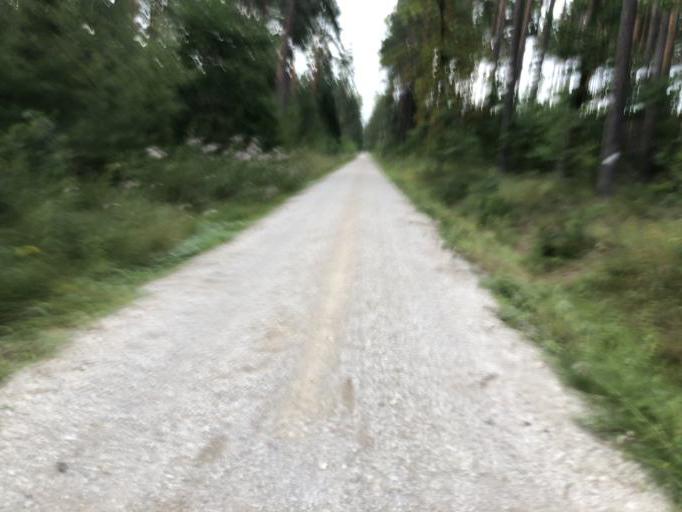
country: DE
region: Bavaria
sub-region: Regierungsbezirk Mittelfranken
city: Uttenreuth
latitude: 49.5794
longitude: 11.0772
